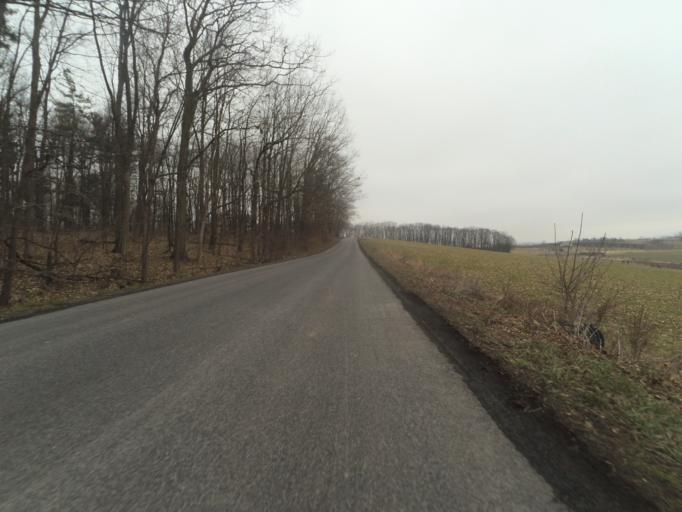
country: US
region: Pennsylvania
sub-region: Centre County
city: Centre Hall
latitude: 40.8595
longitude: -77.6500
